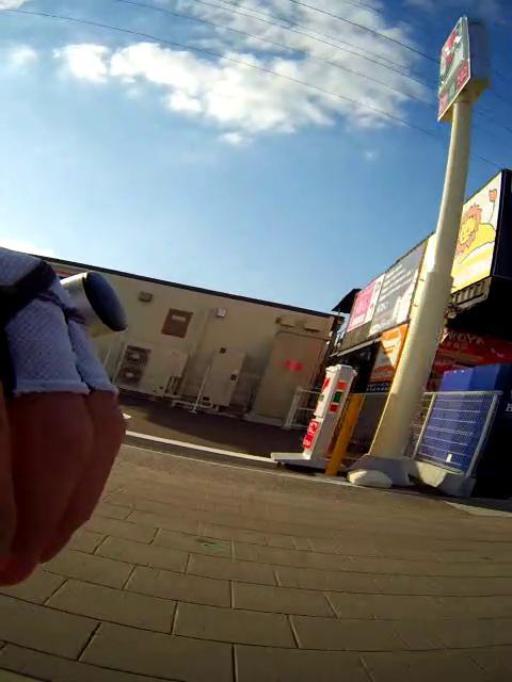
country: JP
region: Hyogo
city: Itami
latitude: 34.7695
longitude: 135.3801
